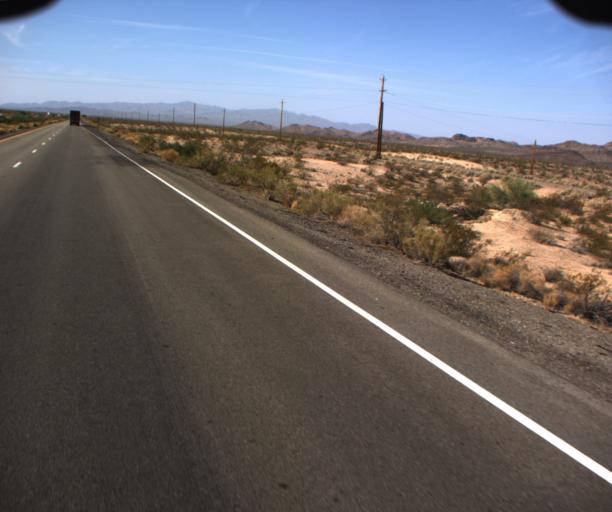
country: US
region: Arizona
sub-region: Mohave County
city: Kingman
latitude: 34.8584
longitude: -114.1469
